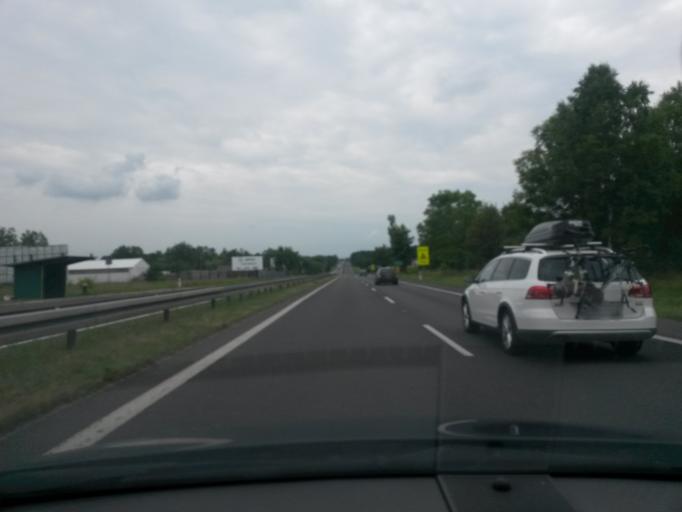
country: PL
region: Lodz Voivodeship
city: Zabia Wola
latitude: 52.0197
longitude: 20.6339
